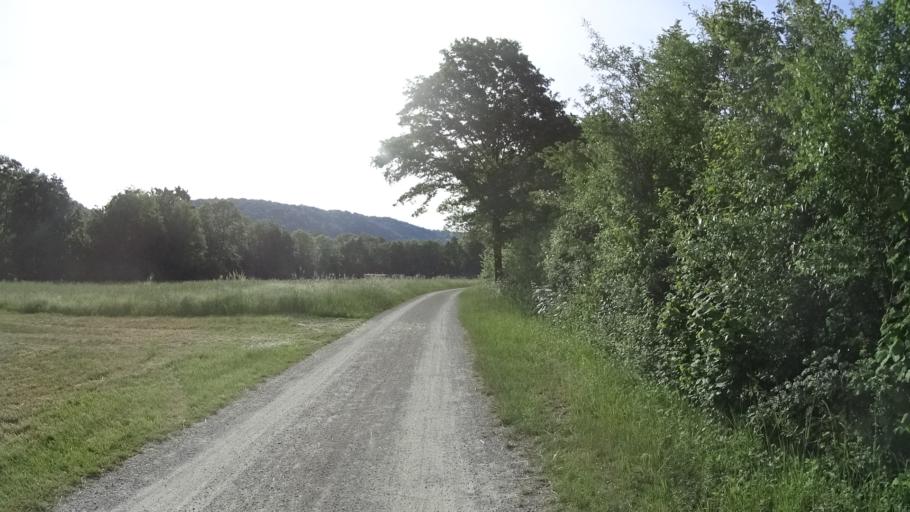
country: DE
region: Bavaria
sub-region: Lower Bavaria
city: Riedenburg
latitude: 48.9545
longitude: 11.7196
